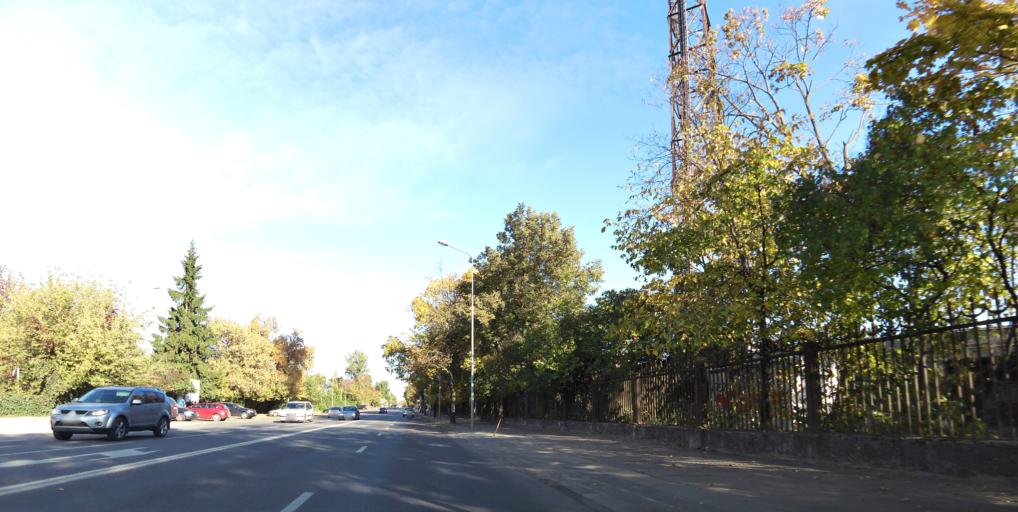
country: LT
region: Vilnius County
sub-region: Vilnius
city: Vilnius
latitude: 54.6923
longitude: 25.2892
